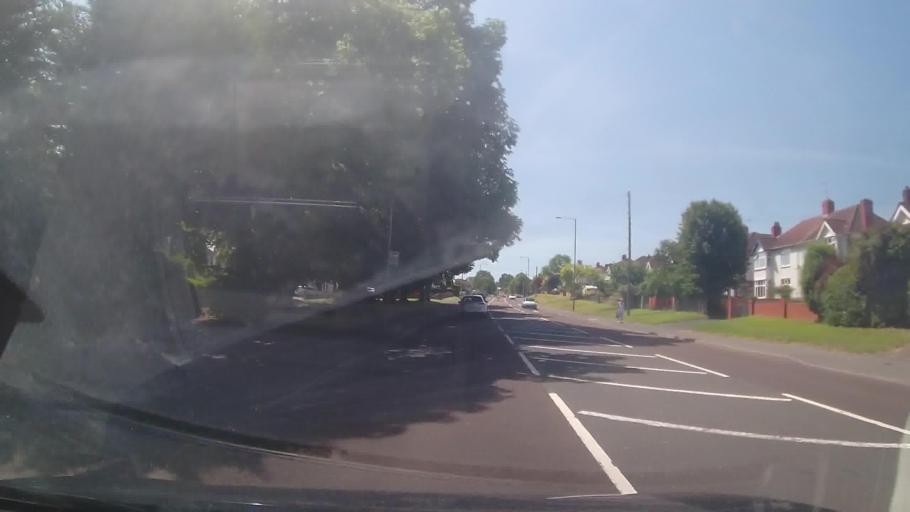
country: GB
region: England
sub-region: Herefordshire
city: Hereford
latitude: 52.0421
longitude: -2.7203
